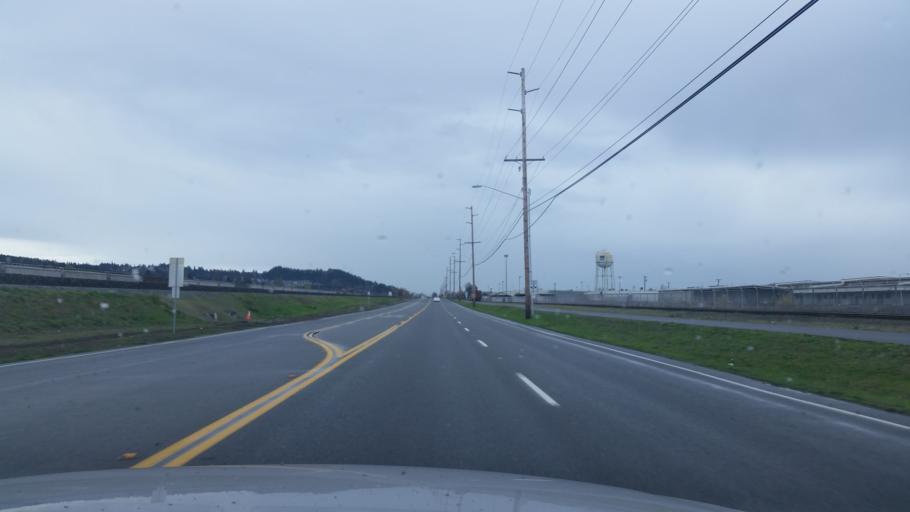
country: US
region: Washington
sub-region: King County
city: Auburn
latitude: 47.2893
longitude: -122.2318
